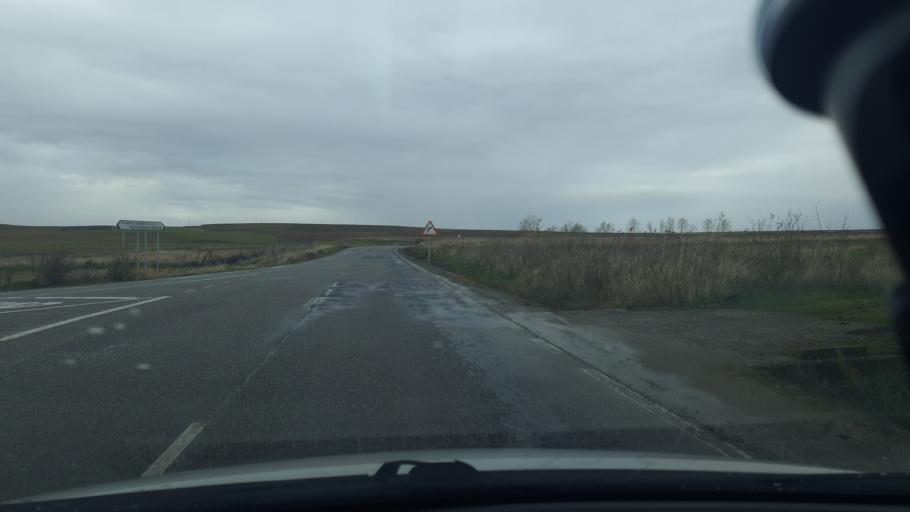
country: ES
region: Castille and Leon
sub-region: Provincia de Segovia
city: Segovia
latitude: 40.9639
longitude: -4.1376
